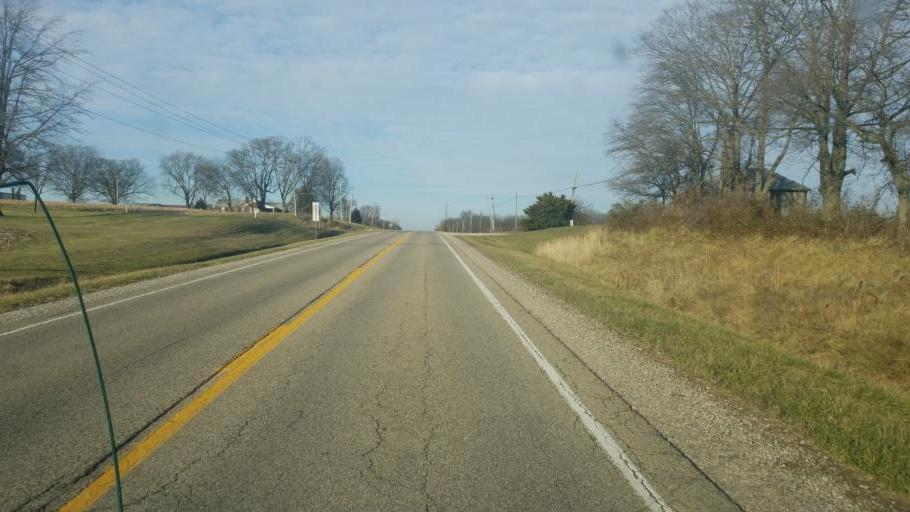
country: US
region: Illinois
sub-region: Lawrence County
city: Lawrenceville
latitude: 38.6571
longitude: -87.6942
